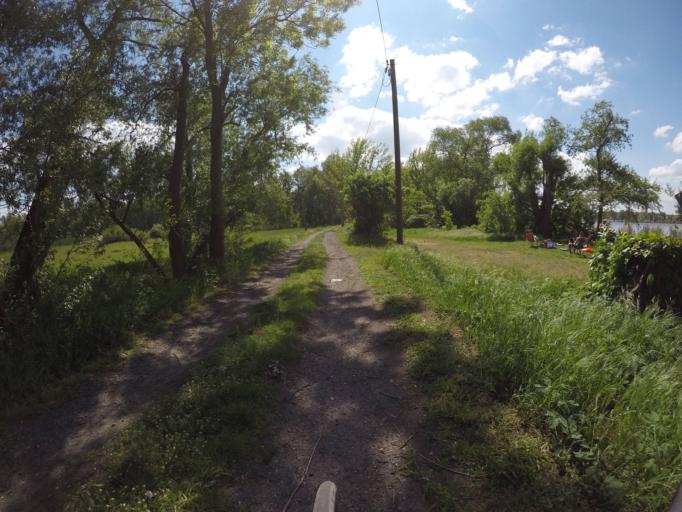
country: DE
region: Brandenburg
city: Werder
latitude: 52.3956
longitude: 12.9403
